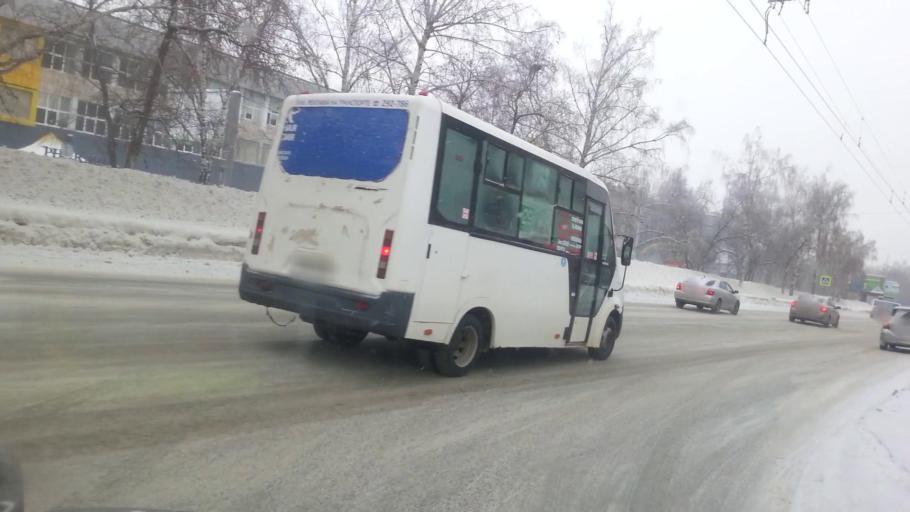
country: RU
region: Altai Krai
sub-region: Gorod Barnaulskiy
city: Barnaul
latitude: 53.3828
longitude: 83.7387
